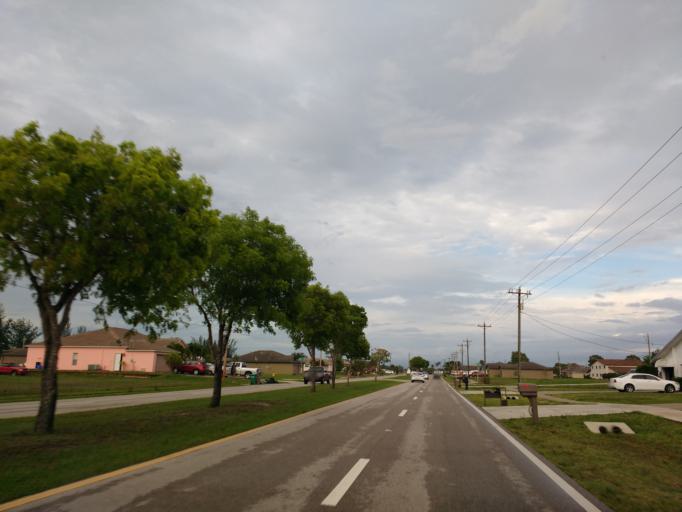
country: US
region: Florida
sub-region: Lee County
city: Cape Coral
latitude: 26.6227
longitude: -82.0024
